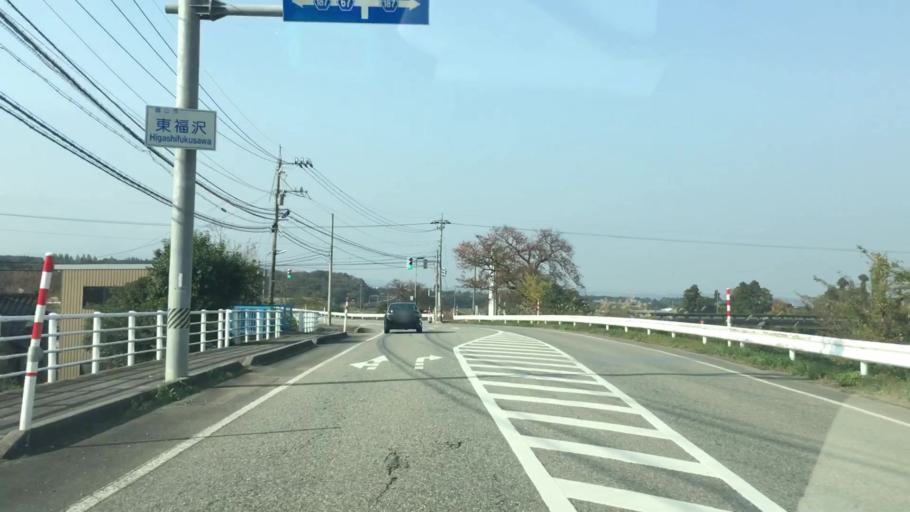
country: JP
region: Toyama
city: Toyama-shi
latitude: 36.6036
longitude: 137.2552
